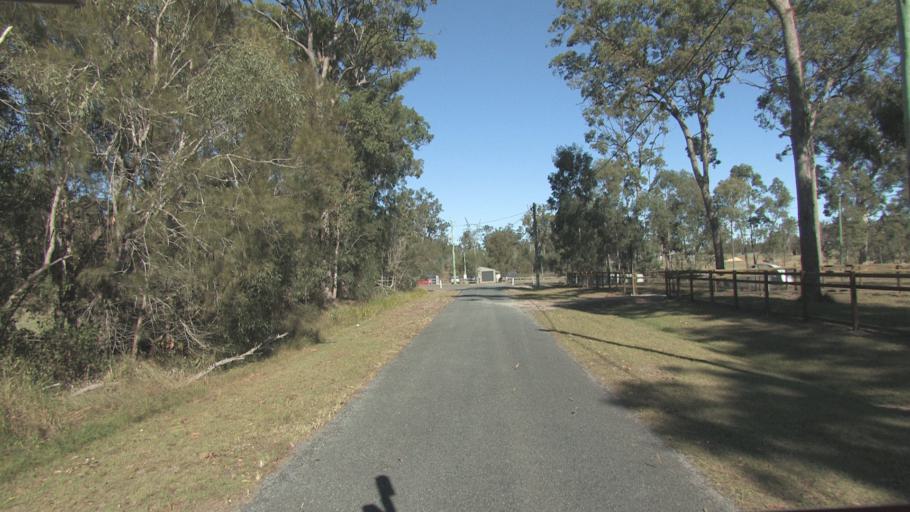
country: AU
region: Queensland
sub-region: Logan
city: Chambers Flat
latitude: -27.7912
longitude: 153.0769
